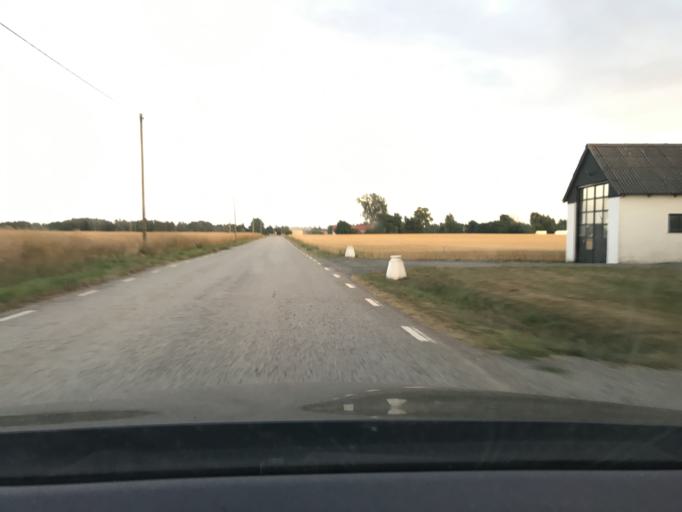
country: SE
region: Skane
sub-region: Simrishamns Kommun
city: Simrishamn
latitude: 55.4407
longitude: 14.2218
